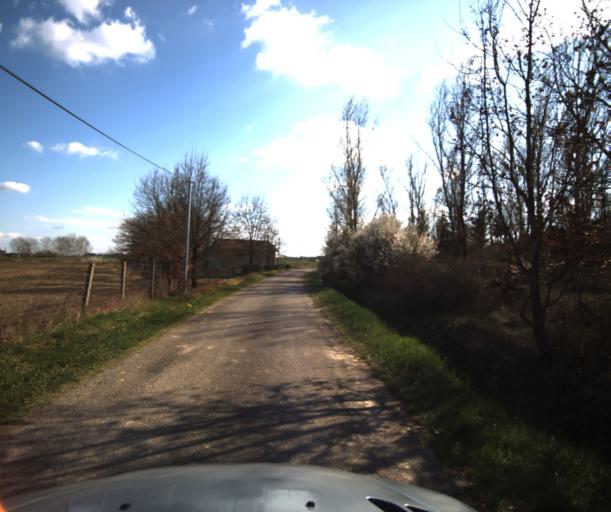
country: FR
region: Midi-Pyrenees
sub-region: Departement du Tarn-et-Garonne
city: Bressols
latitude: 43.9636
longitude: 1.2877
